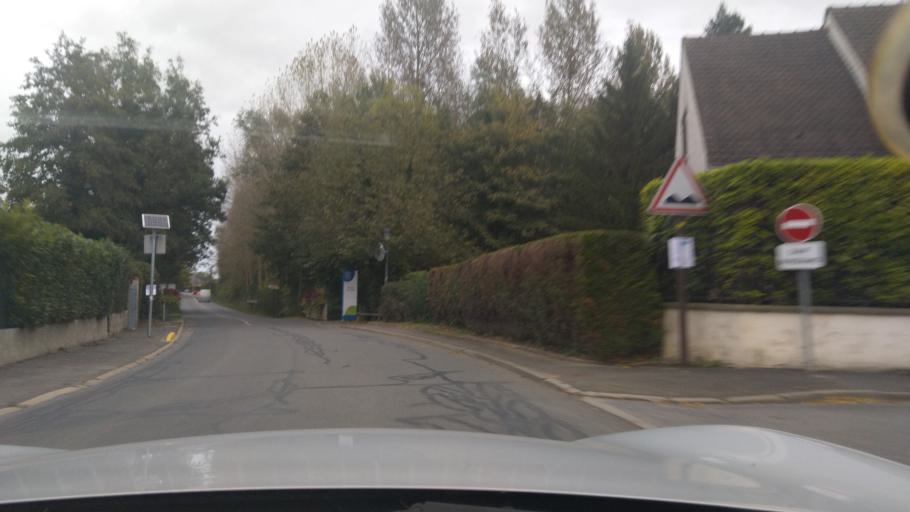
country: FR
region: Ile-de-France
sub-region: Departement de Seine-et-Marne
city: Claye-Souilly
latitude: 48.9646
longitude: 2.6767
